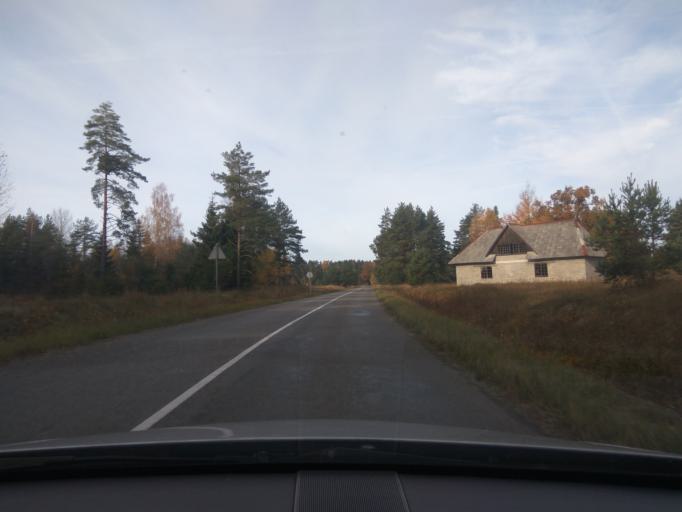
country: LV
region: Alsunga
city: Alsunga
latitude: 56.9883
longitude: 21.5060
